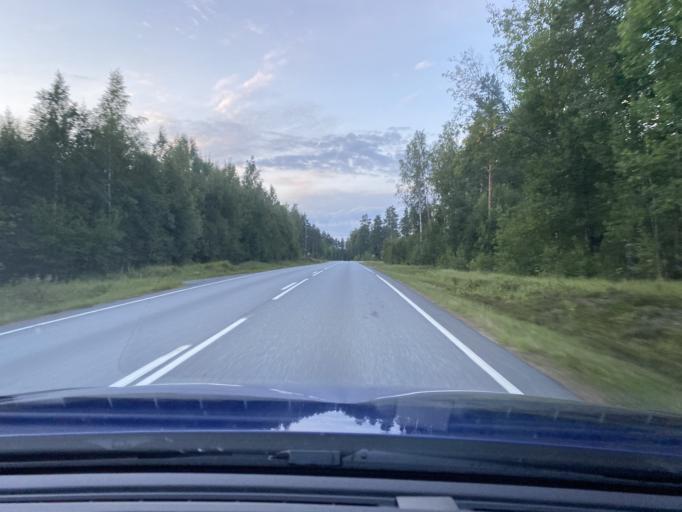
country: FI
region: Satakunta
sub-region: Pohjois-Satakunta
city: Honkajoki
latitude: 62.0406
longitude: 22.2421
